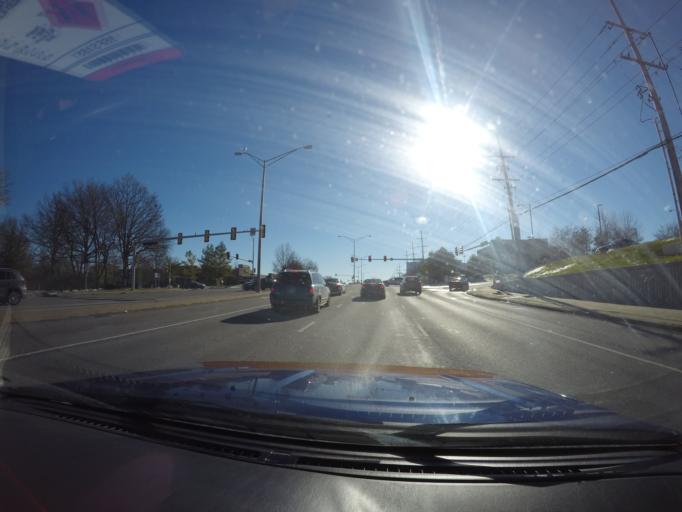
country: US
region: Kansas
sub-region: Johnson County
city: Leawood
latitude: 38.9298
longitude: -94.6490
